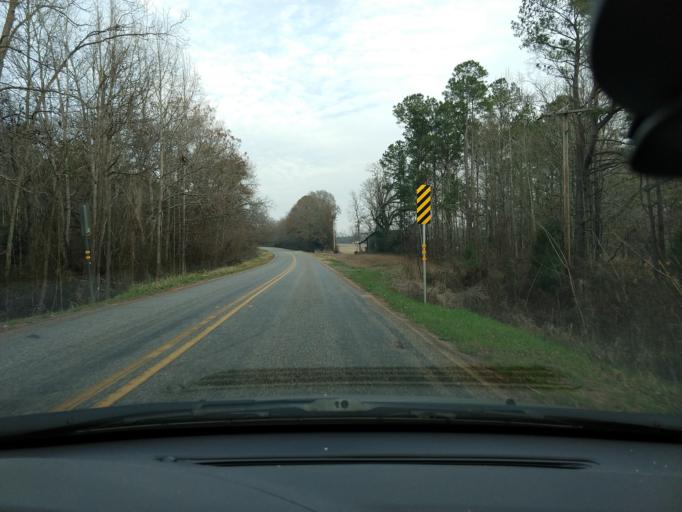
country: US
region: Georgia
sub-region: Webster County
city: Preston
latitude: 32.0140
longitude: -84.4096
